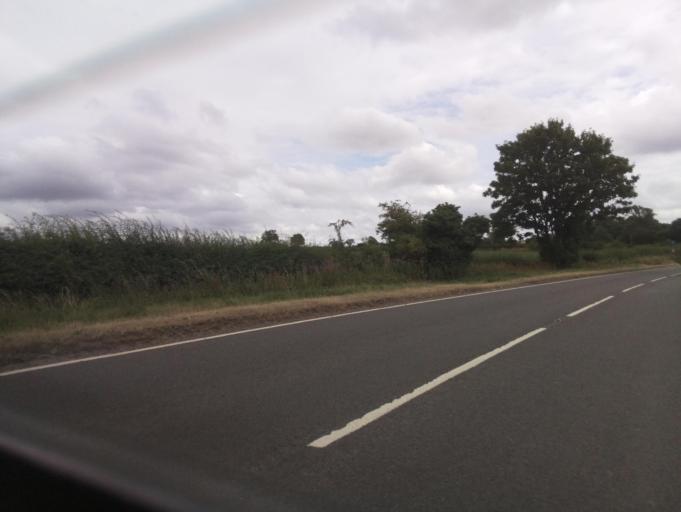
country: GB
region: England
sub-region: Leicestershire
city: Castle Donington
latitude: 52.8078
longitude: -1.3765
